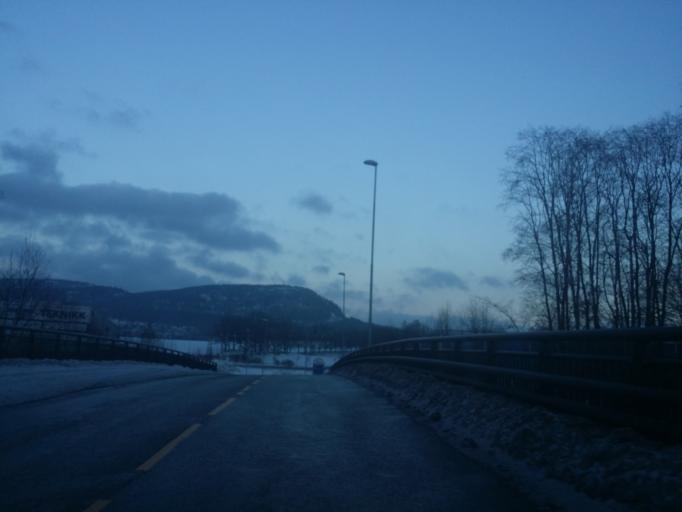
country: NO
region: Akershus
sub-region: Baerum
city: Skui
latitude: 59.9117
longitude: 10.4730
